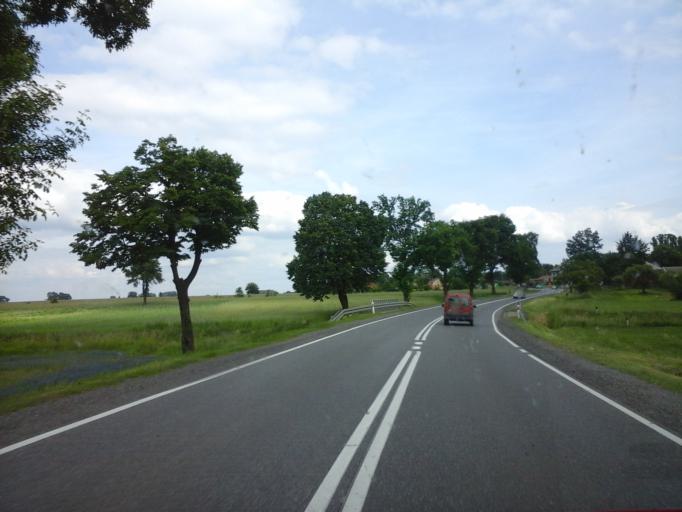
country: PL
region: Lodz Voivodeship
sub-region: Powiat opoczynski
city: Paradyz
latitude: 51.3158
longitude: 20.0660
